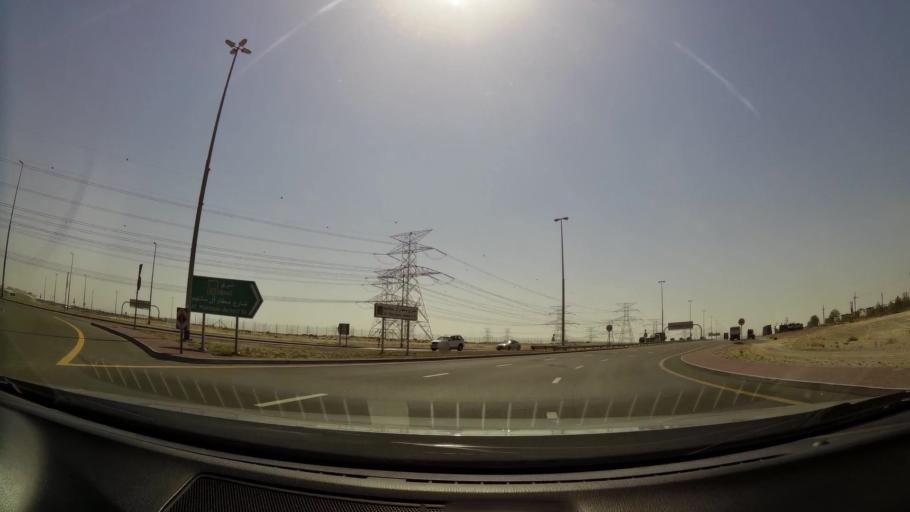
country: AE
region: Dubai
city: Dubai
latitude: 24.9365
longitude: 55.0766
